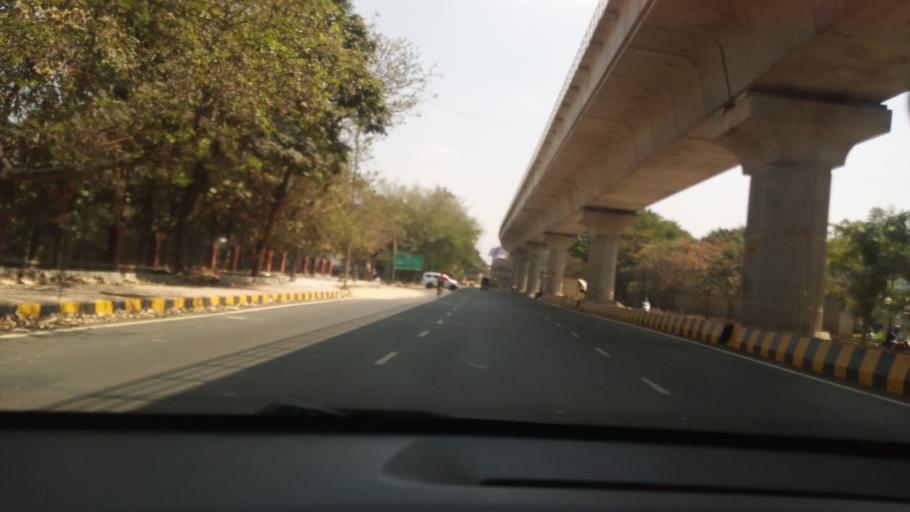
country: IN
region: Karnataka
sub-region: Bangalore Rural
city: Hoskote
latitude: 12.9771
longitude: 77.7210
